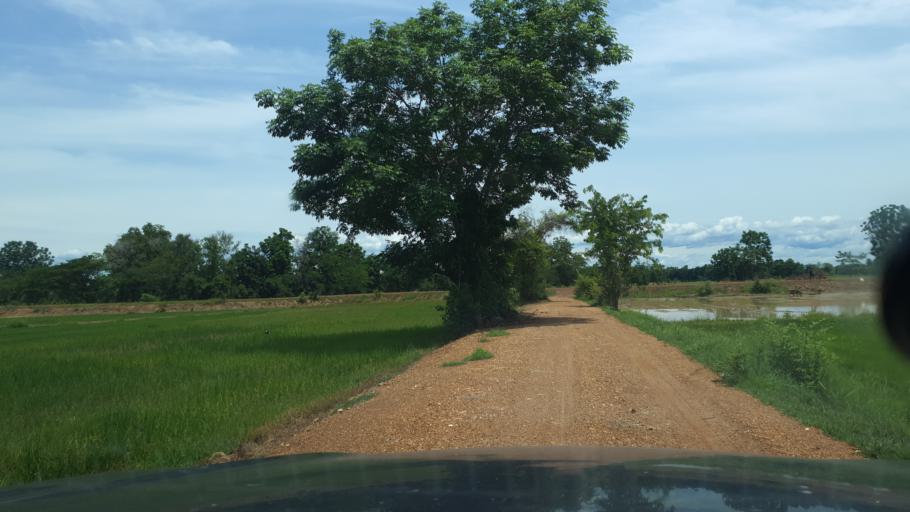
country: TH
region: Sukhothai
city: Ban Na
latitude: 17.0794
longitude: 99.6928
